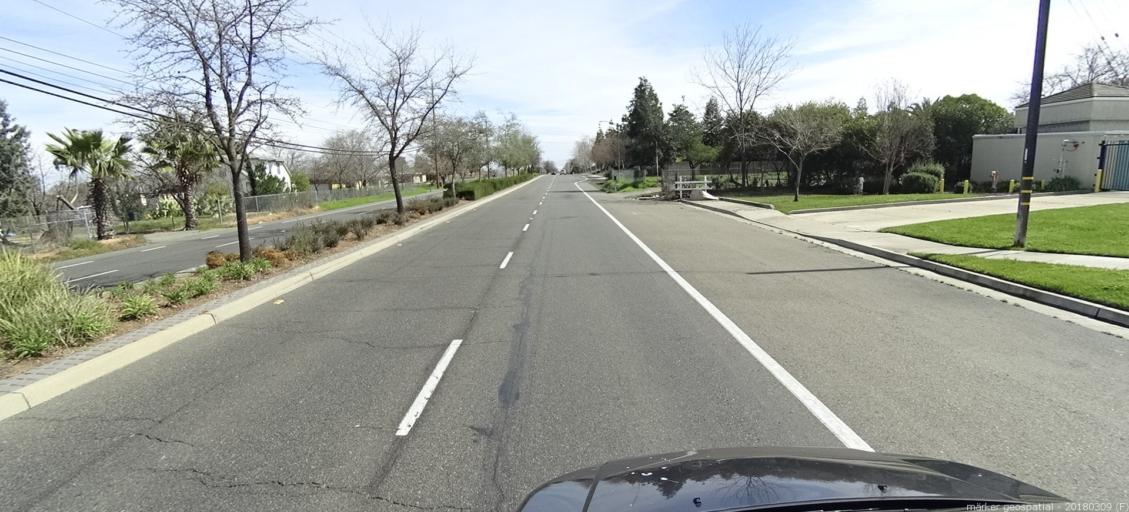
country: US
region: California
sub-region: Sacramento County
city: Vineyard
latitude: 38.4526
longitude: -121.3683
